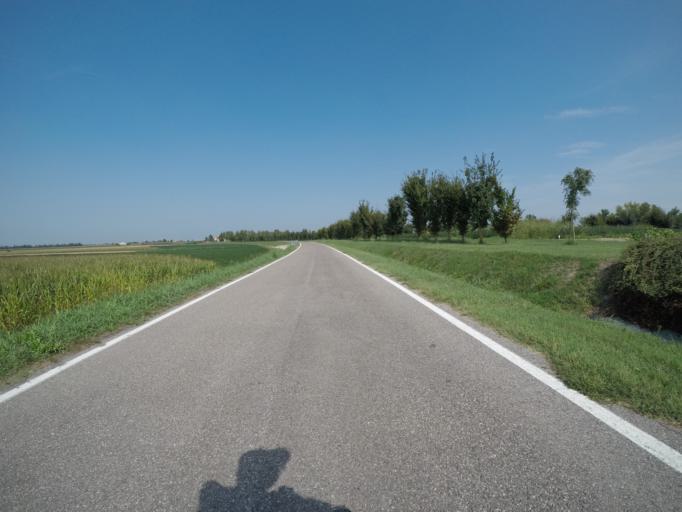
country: IT
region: Veneto
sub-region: Provincia di Rovigo
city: Villanova del Ghebbo Canton
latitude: 45.0628
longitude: 11.6238
